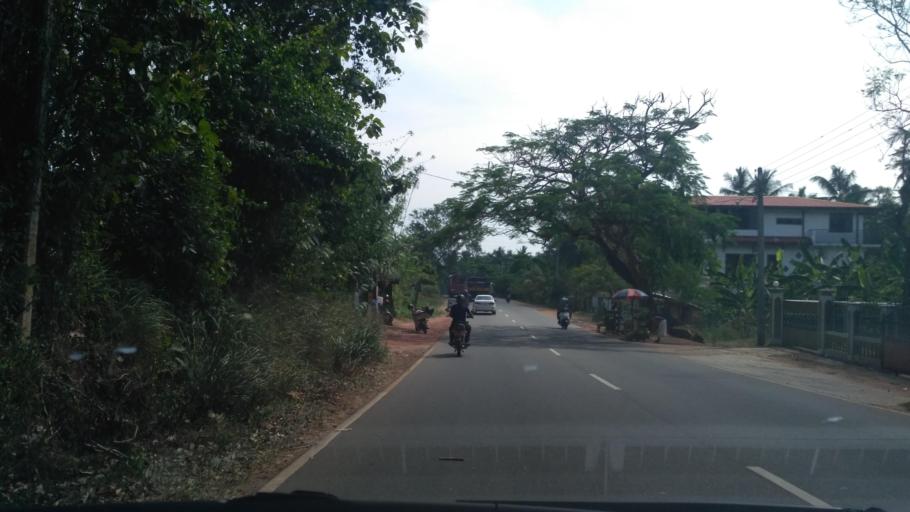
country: LK
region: North Western
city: Kuliyapitiya
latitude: 7.3402
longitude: 80.0304
